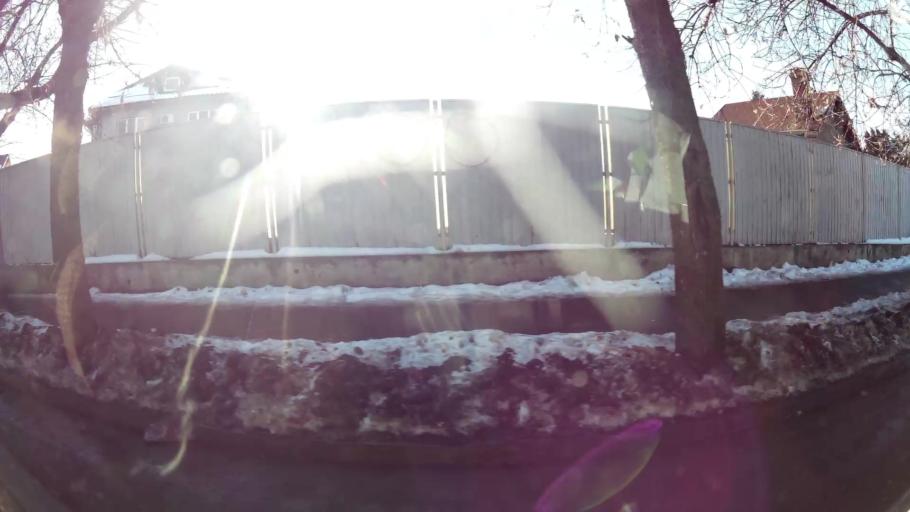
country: RO
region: Bucuresti
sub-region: Municipiul Bucuresti
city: Bucuresti
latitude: 44.3855
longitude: 26.0795
